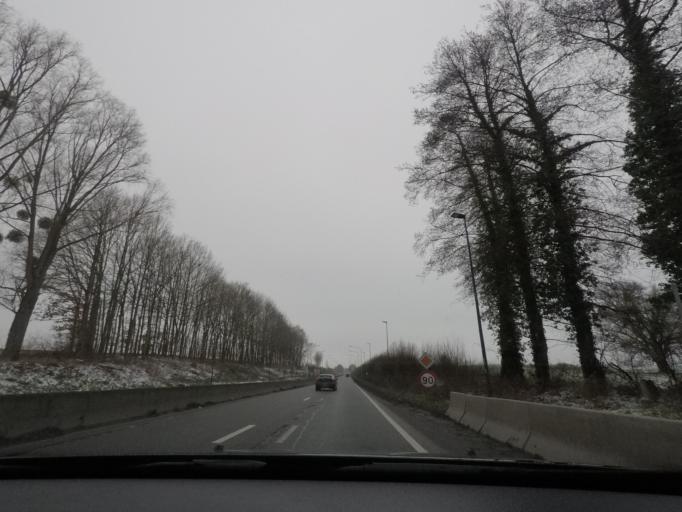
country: BE
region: Wallonia
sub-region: Province de Namur
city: Sombreffe
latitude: 50.4720
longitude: 4.6209
